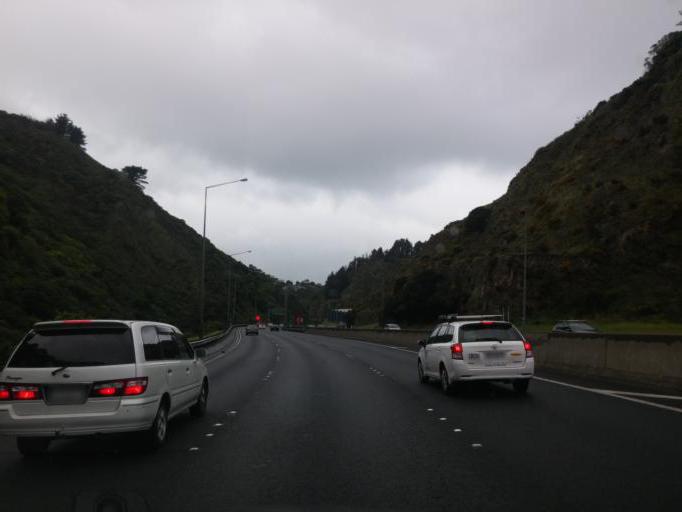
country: NZ
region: Wellington
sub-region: Wellington City
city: Wellington
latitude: -41.2389
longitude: 174.8066
